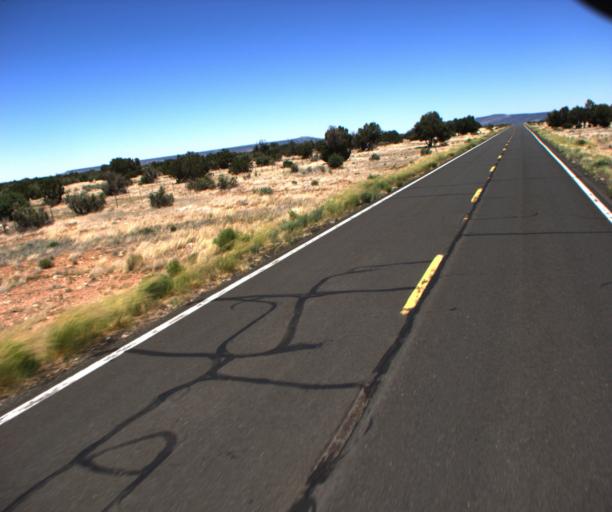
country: US
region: Arizona
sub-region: Coconino County
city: LeChee
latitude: 34.7445
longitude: -111.0490
